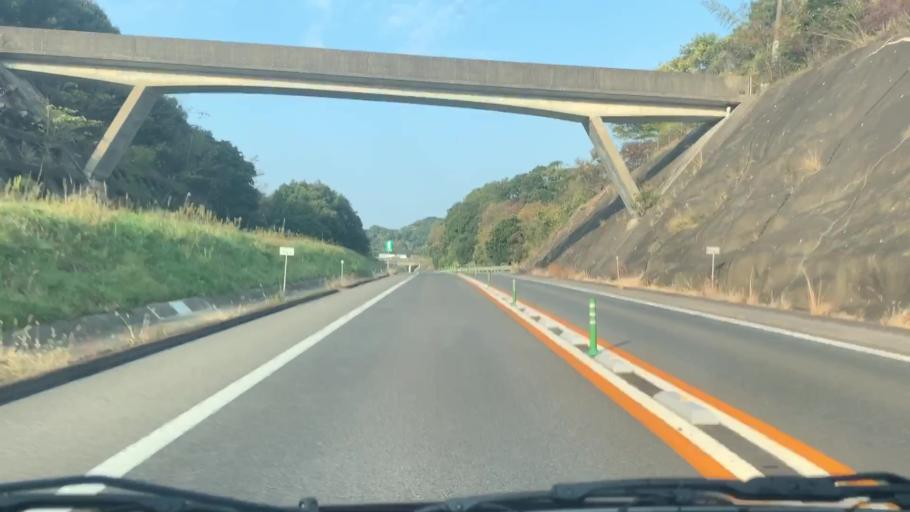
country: JP
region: Nagasaki
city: Sasebo
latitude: 33.1507
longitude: 129.8024
